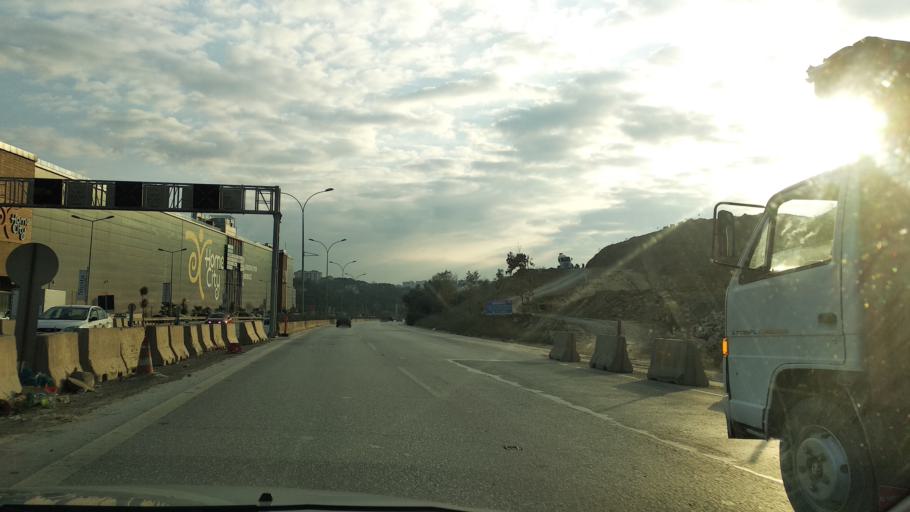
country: TR
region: Istanbul
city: Icmeler
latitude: 40.8889
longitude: 29.3249
